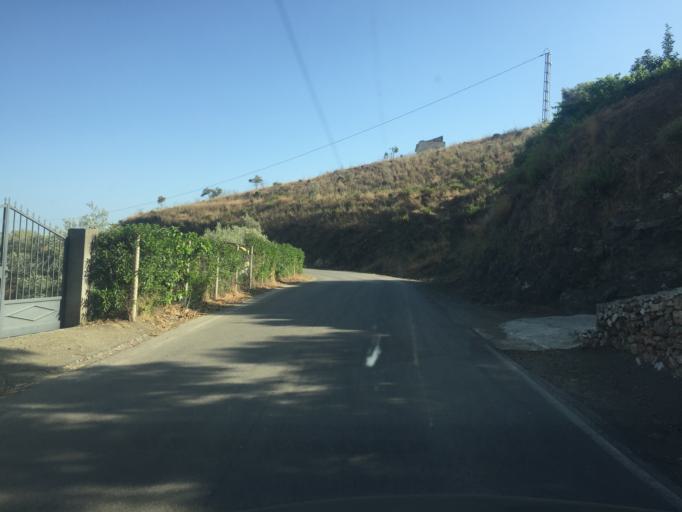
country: ES
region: Andalusia
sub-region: Provincia de Malaga
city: Frigiliana
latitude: 36.8048
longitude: -3.9171
